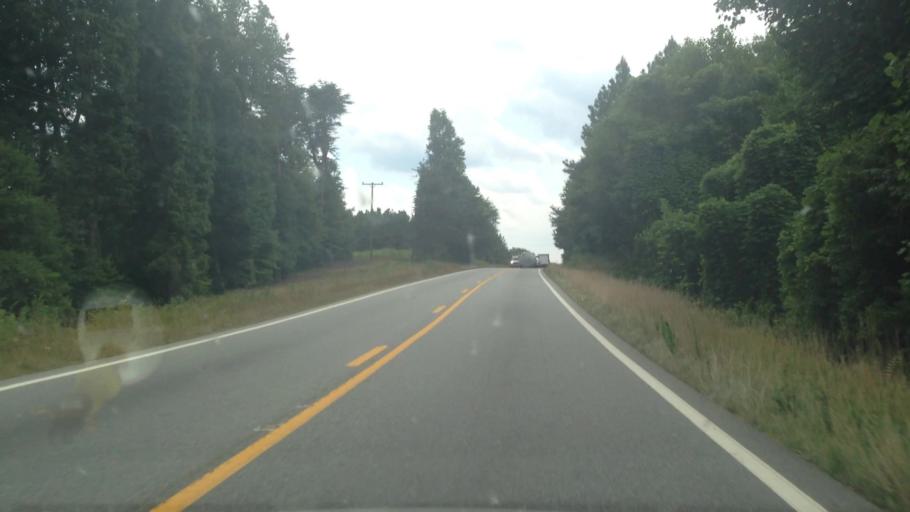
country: US
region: North Carolina
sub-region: Guilford County
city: Stokesdale
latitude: 36.2707
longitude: -79.9467
